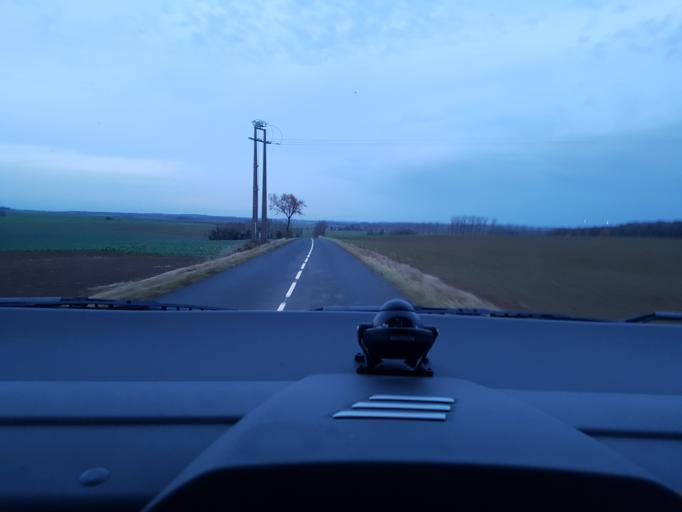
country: FR
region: Picardie
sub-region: Departement de la Somme
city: Beauquesne
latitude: 50.0736
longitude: 2.4215
